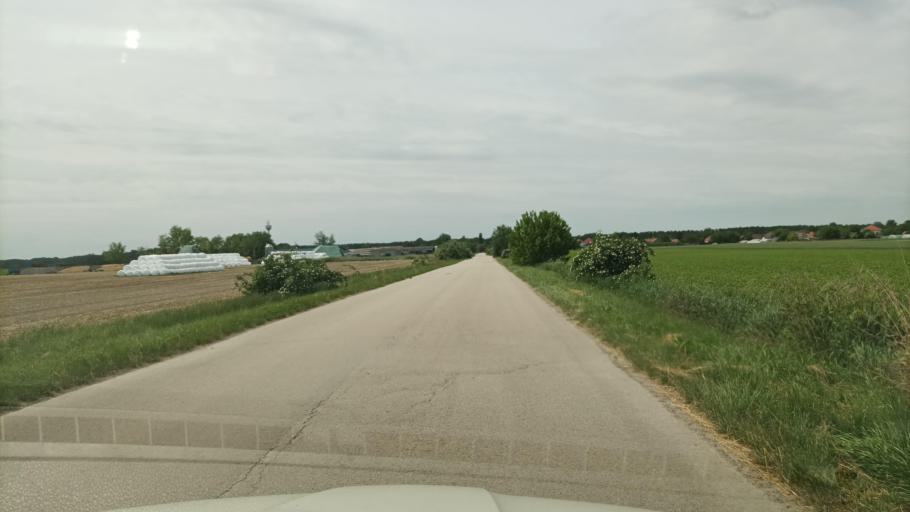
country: HU
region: Fejer
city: Adony
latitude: 47.1179
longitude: 18.9073
